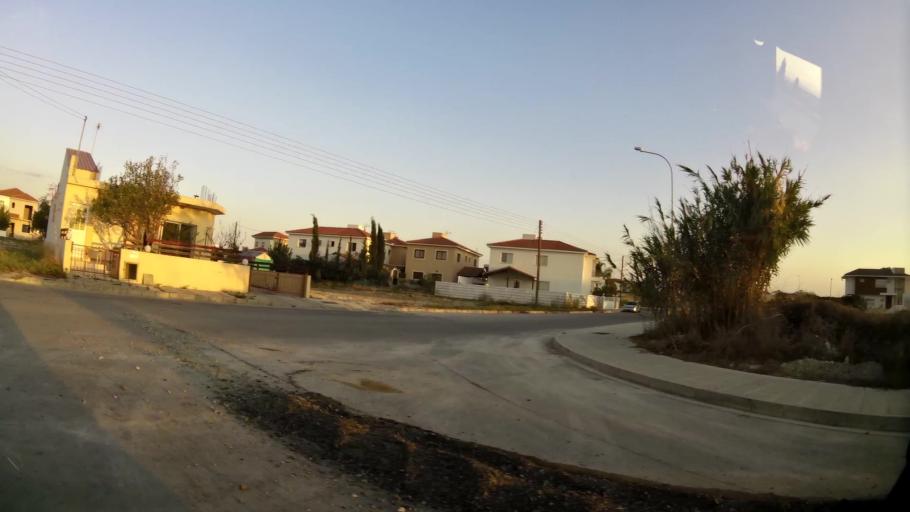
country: CY
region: Larnaka
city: Aradippou
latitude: 34.9173
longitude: 33.5836
